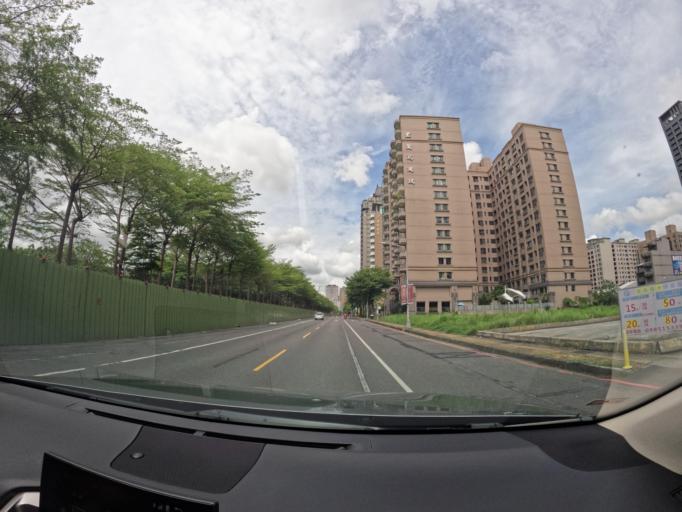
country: TW
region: Kaohsiung
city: Kaohsiung
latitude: 22.6549
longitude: 120.2837
